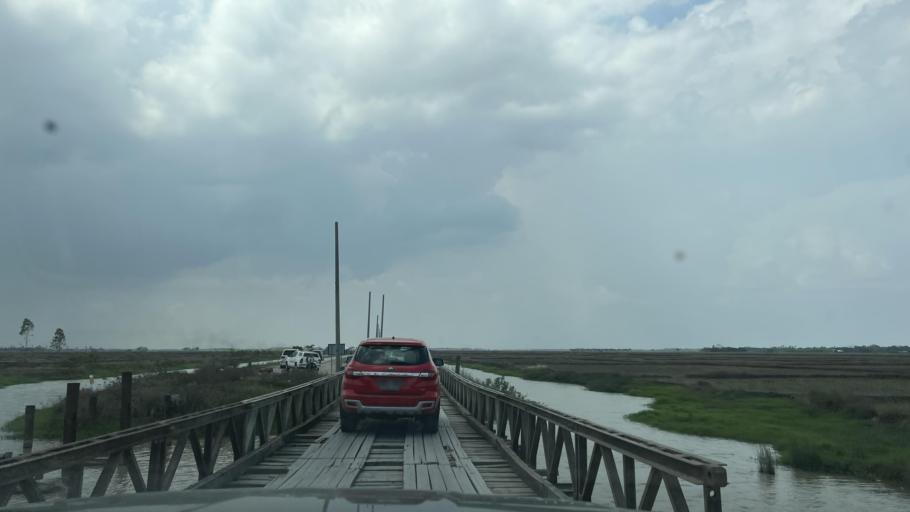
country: MM
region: Ayeyarwady
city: Pyapon
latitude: 16.0687
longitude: 95.6187
